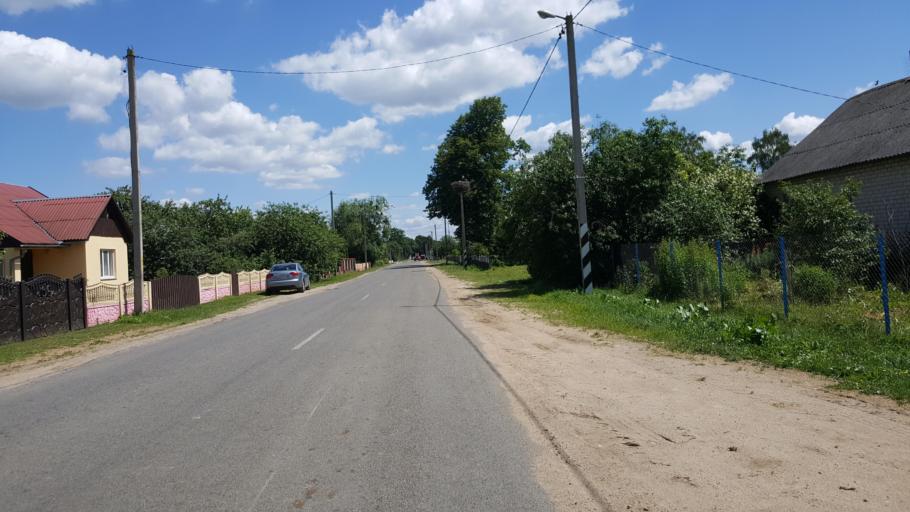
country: PL
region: Podlasie
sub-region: Powiat hajnowski
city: Czeremcha
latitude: 52.4902
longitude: 23.4437
